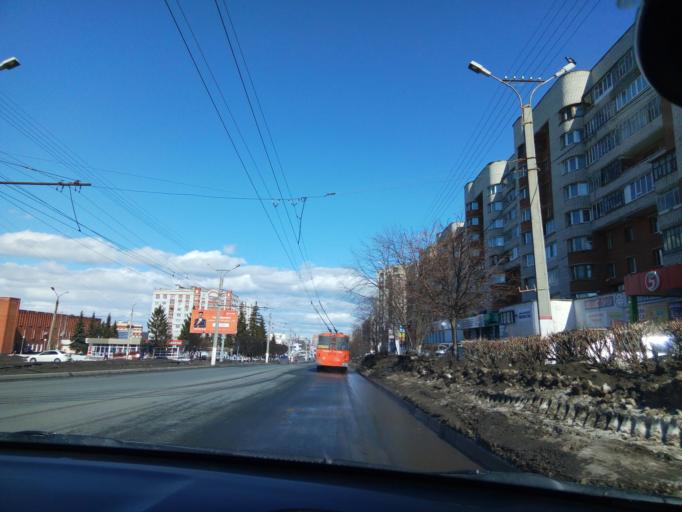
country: RU
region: Chuvashia
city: Novyye Lapsary
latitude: 56.1165
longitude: 47.1815
